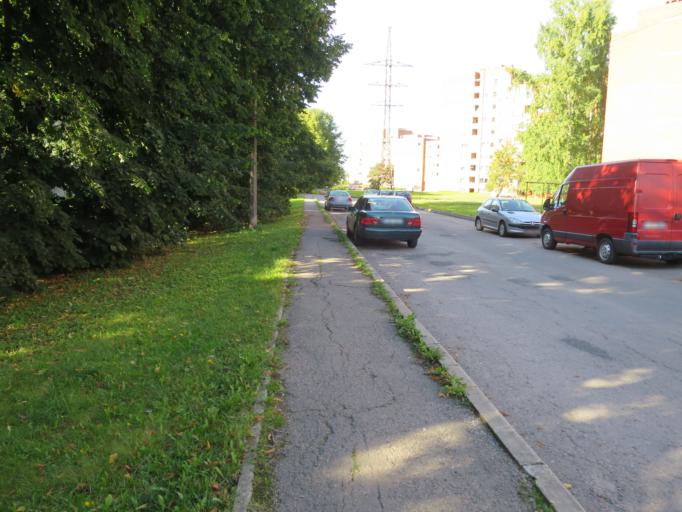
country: EE
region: Harju
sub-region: Tallinna linn
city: Tallinn
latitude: 59.4065
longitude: 24.7074
